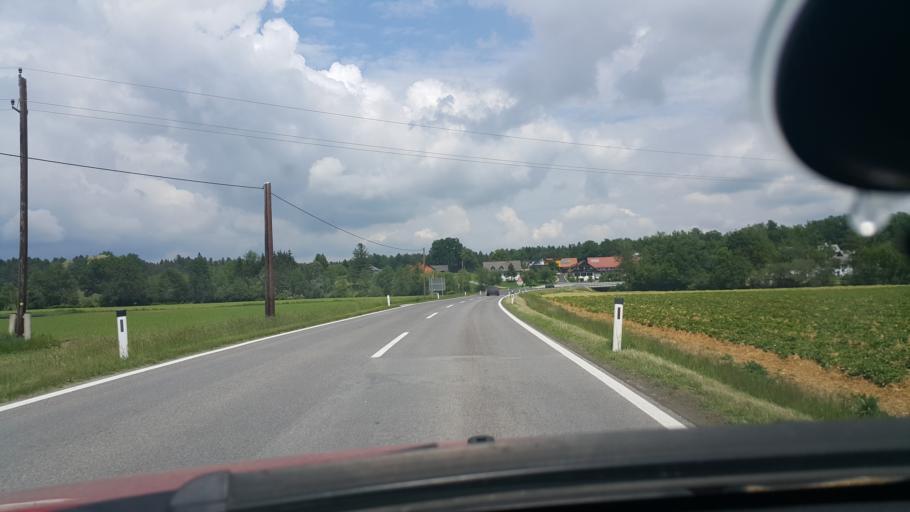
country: AT
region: Styria
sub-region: Politischer Bezirk Deutschlandsberg
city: Sankt Martin im Sulmtal
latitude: 46.7479
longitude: 15.3270
